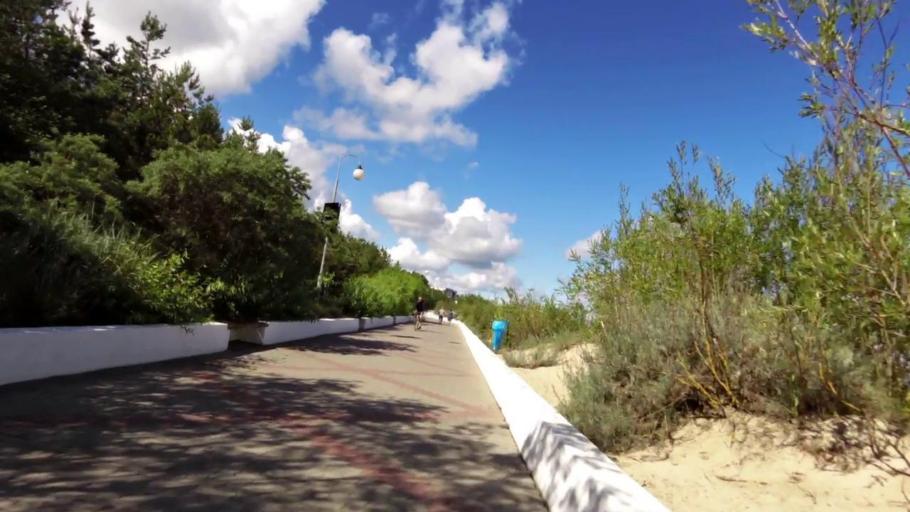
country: PL
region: West Pomeranian Voivodeship
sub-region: Powiat koszalinski
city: Mielno
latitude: 54.2640
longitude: 16.0601
